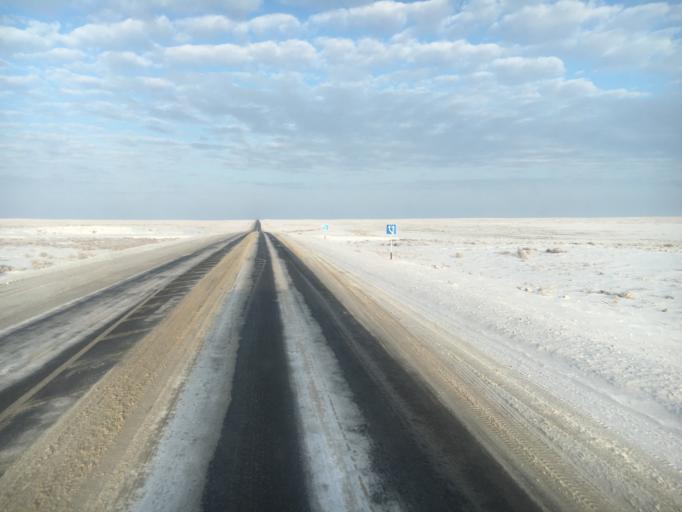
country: KZ
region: Qyzylorda
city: Sekseuil
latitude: 47.6792
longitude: 61.4428
